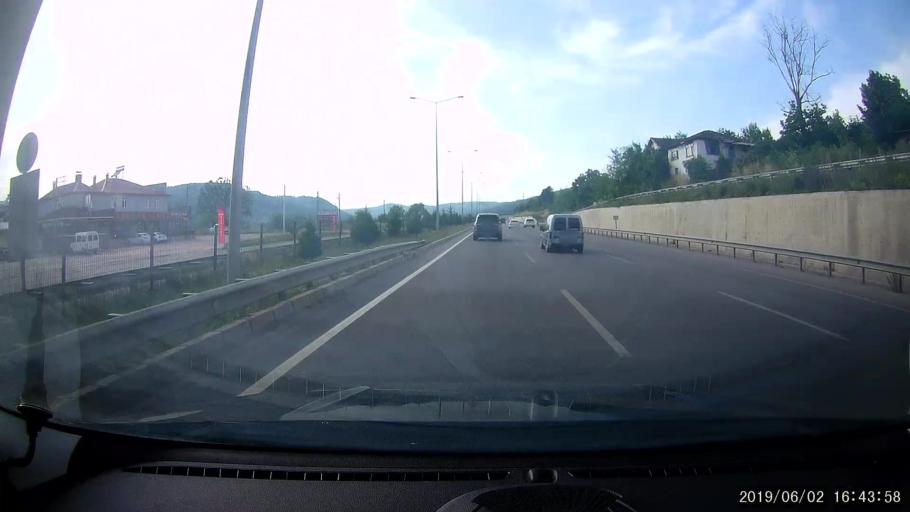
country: TR
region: Samsun
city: Kavak
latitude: 41.1434
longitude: 36.1177
